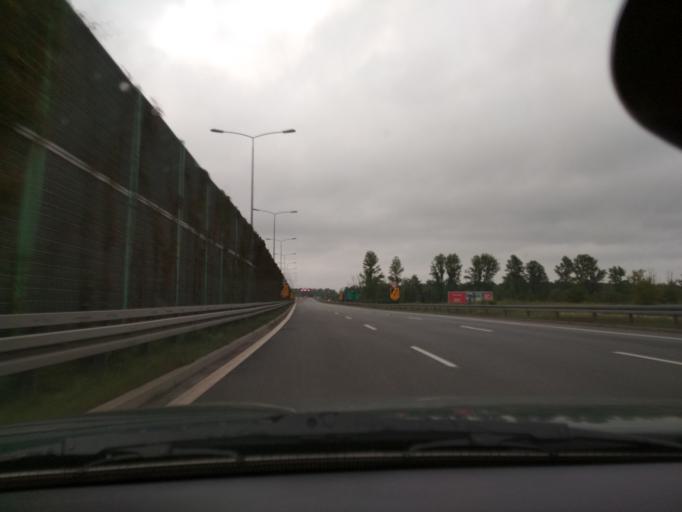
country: PL
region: Silesian Voivodeship
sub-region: Powiat gliwicki
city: Przyszowice
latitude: 50.2807
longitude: 18.7360
